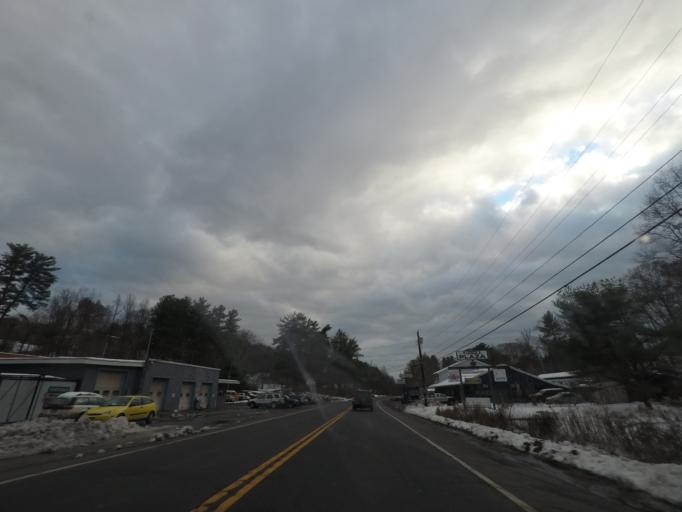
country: US
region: New York
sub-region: Ulster County
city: Rosendale Village
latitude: 41.8568
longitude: -74.0721
